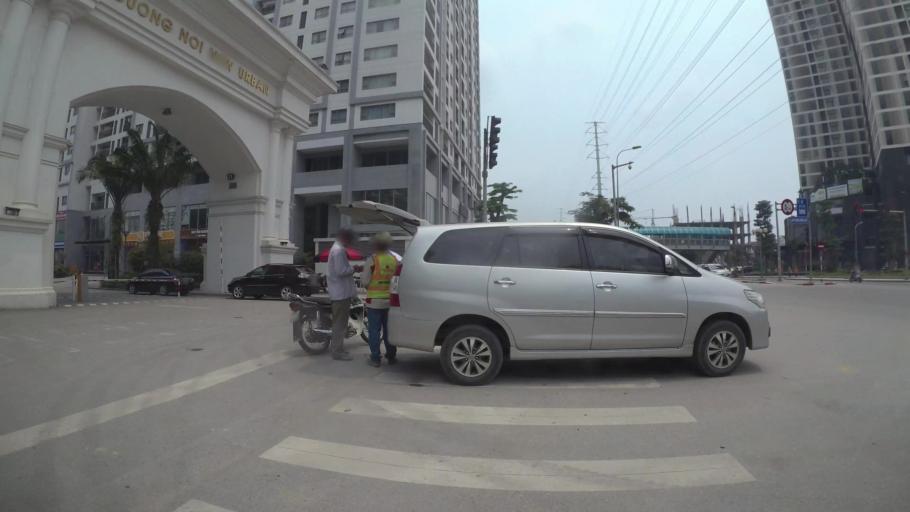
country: VN
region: Ha Noi
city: Ha Dong
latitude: 20.9762
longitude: 105.7613
